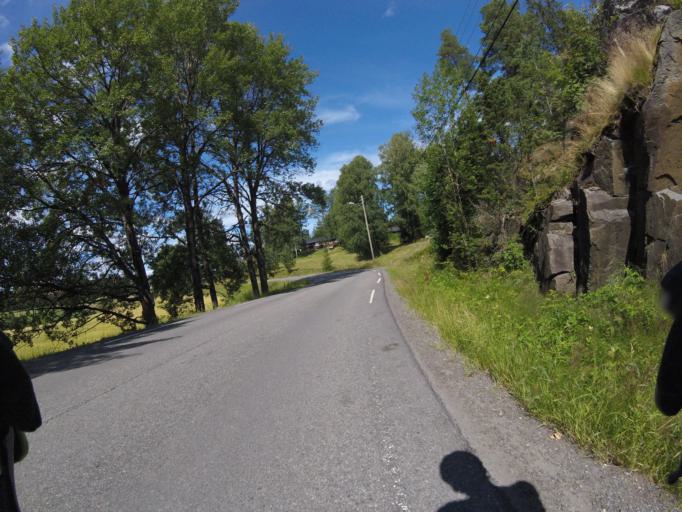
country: NO
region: Akershus
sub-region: Lorenskog
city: Kjenn
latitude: 59.9071
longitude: 10.9601
